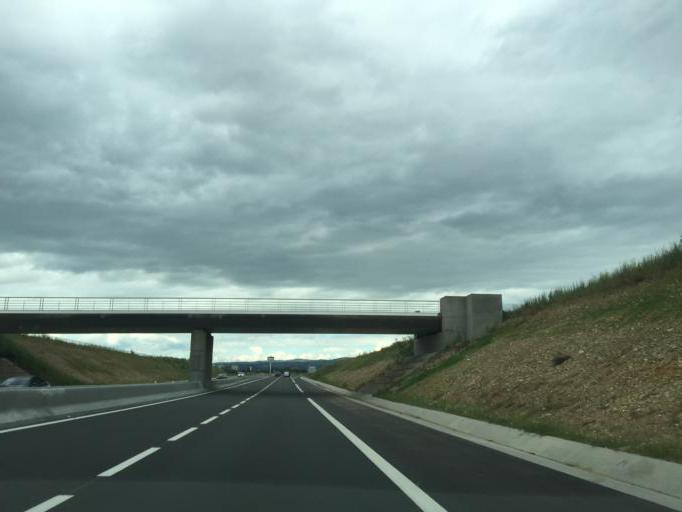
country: FR
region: Rhone-Alpes
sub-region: Departement de la Loire
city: Bonson
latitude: 45.5138
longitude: 4.2231
